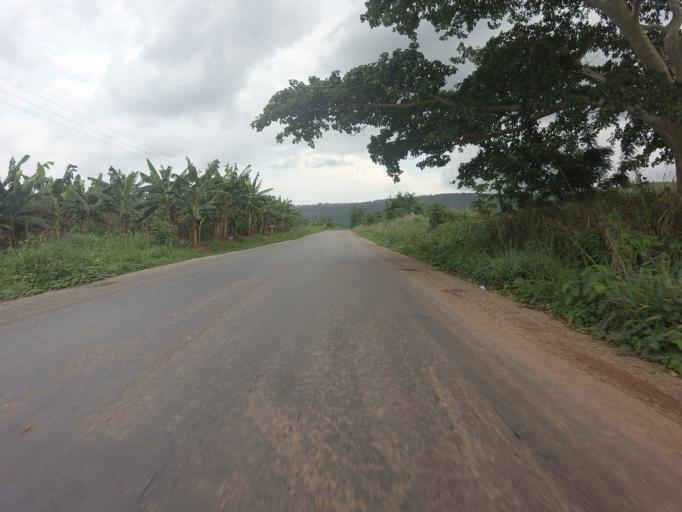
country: GH
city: Akropong
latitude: 5.9610
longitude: -0.1376
